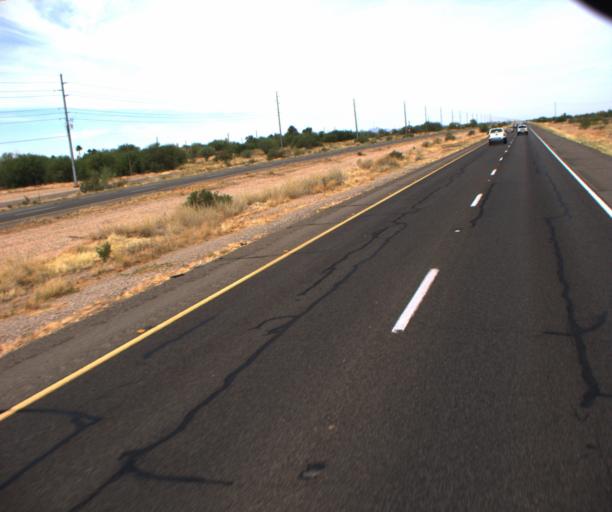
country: US
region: Arizona
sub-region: Maricopa County
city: Sun City West
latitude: 33.7086
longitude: -112.4397
